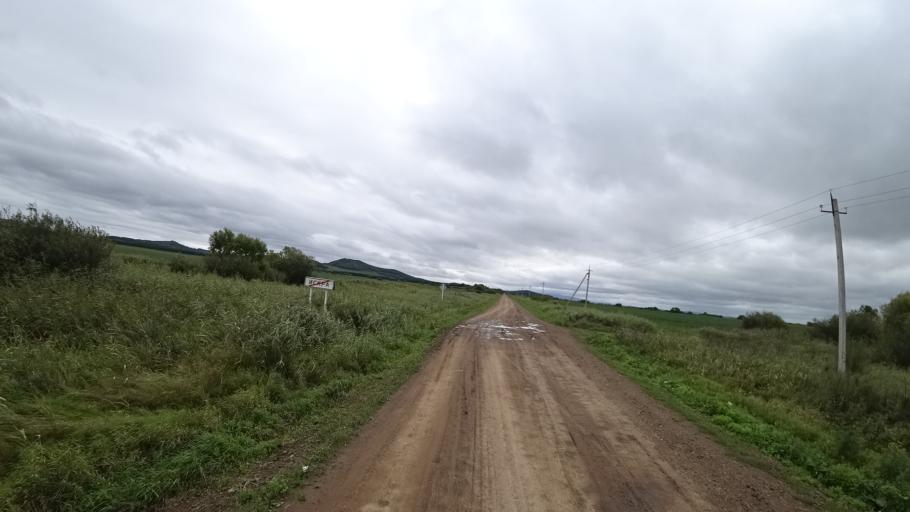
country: RU
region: Primorskiy
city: Chernigovka
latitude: 44.4941
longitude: 132.5712
